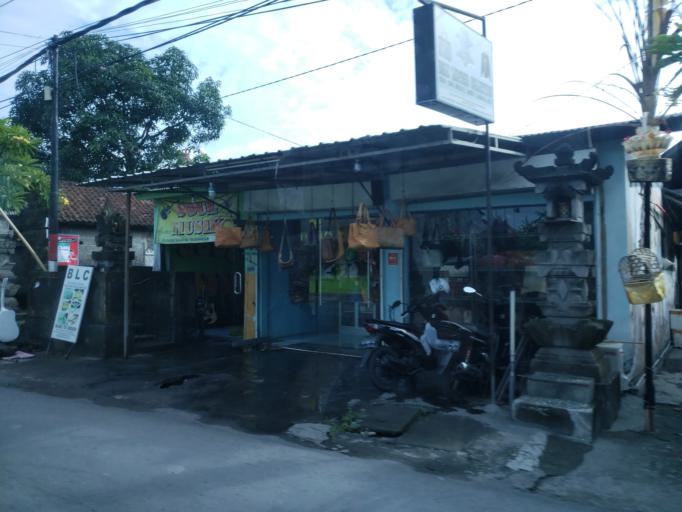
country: ID
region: Bali
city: Denpasar
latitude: -8.6742
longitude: 115.1813
